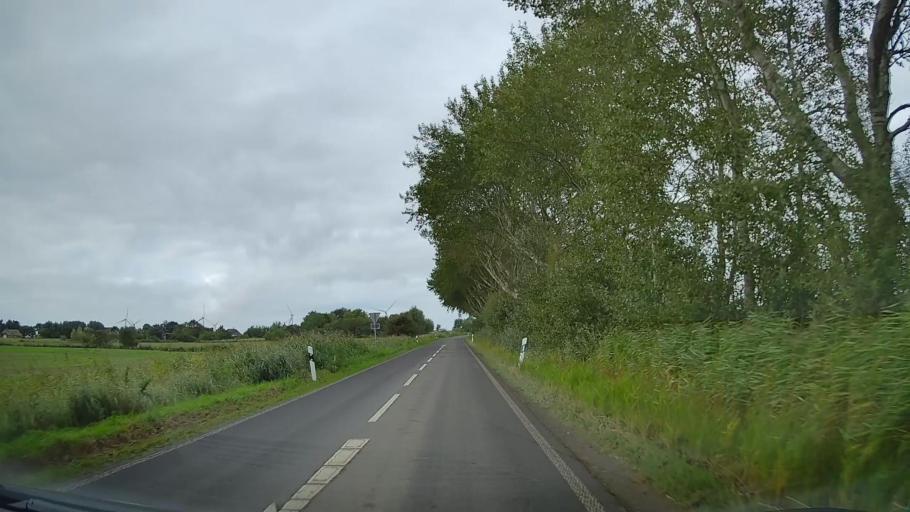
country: DE
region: Schleswig-Holstein
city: Friedrich-Wilhelm-Lubke-Koog
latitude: 54.8356
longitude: 8.6605
